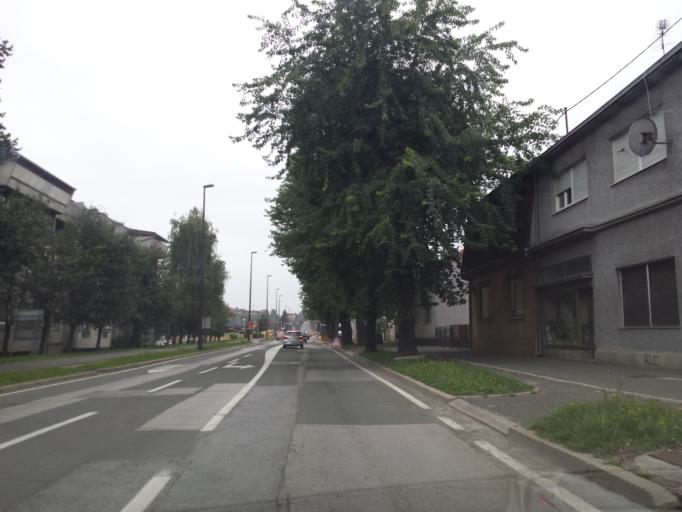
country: HR
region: Karlovacka
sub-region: Grad Karlovac
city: Karlovac
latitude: 45.4849
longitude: 15.5475
